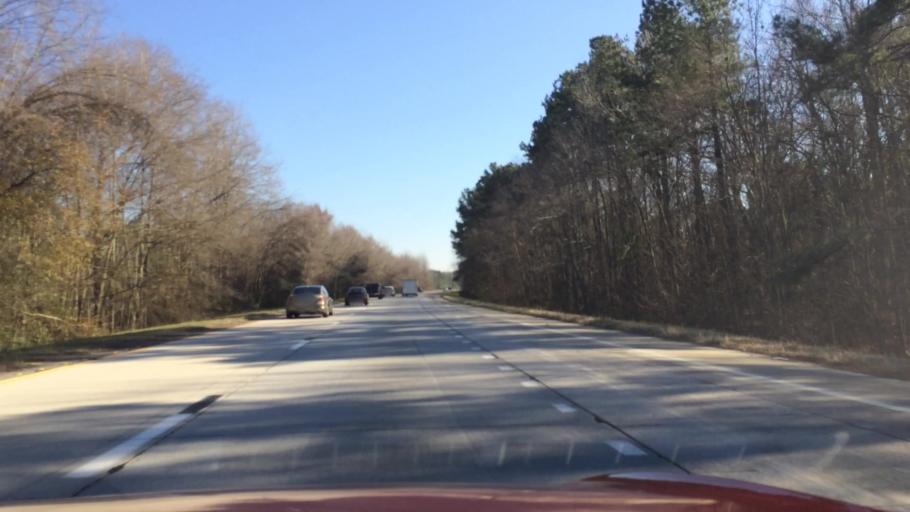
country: US
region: South Carolina
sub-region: Orangeburg County
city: Holly Hill
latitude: 33.2657
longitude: -80.4823
